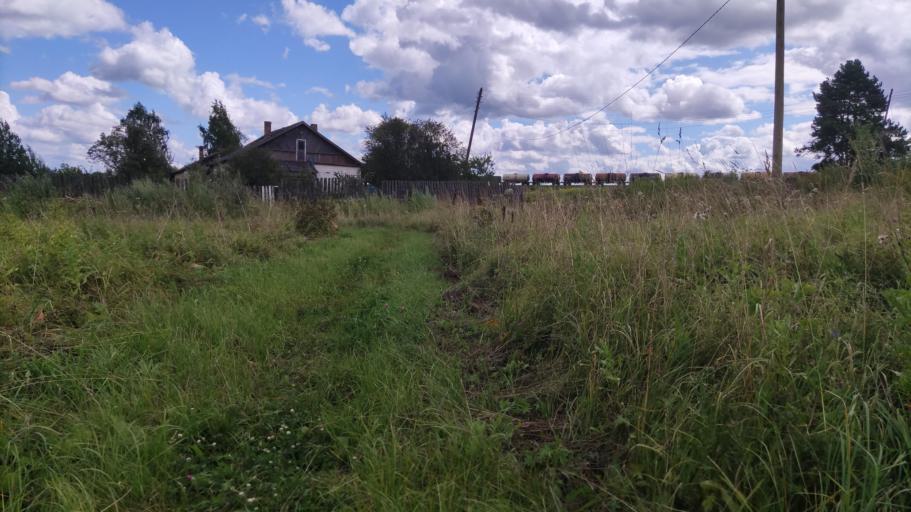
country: RU
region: Tverskaya
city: Rzhev
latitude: 56.2401
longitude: 34.2961
